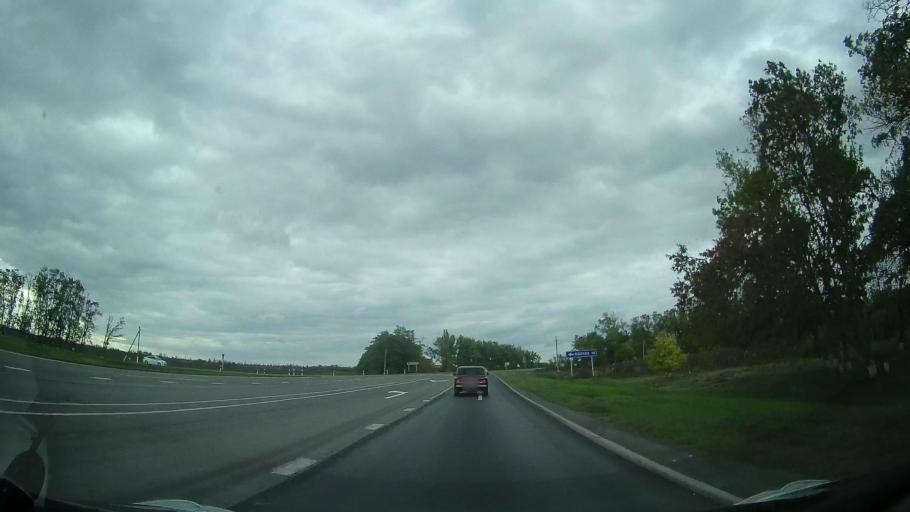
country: RU
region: Rostov
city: Yegorlykskaya
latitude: 46.5372
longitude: 40.7822
